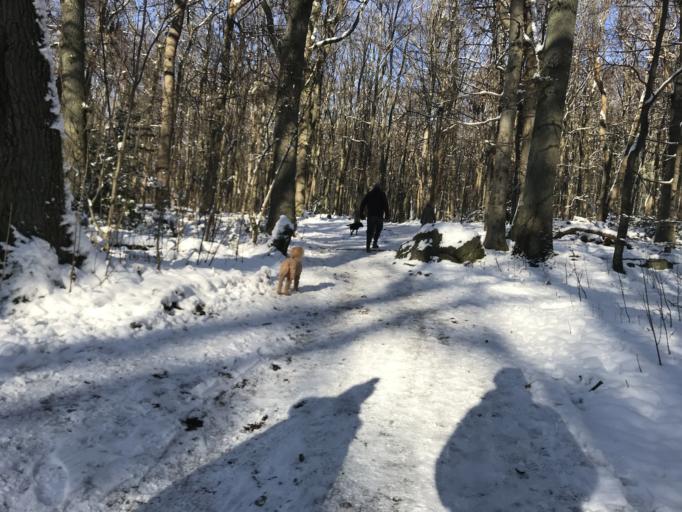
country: DE
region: Hesse
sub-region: Regierungsbezirk Darmstadt
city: Konigstein im Taunus
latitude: 50.1847
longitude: 8.4749
